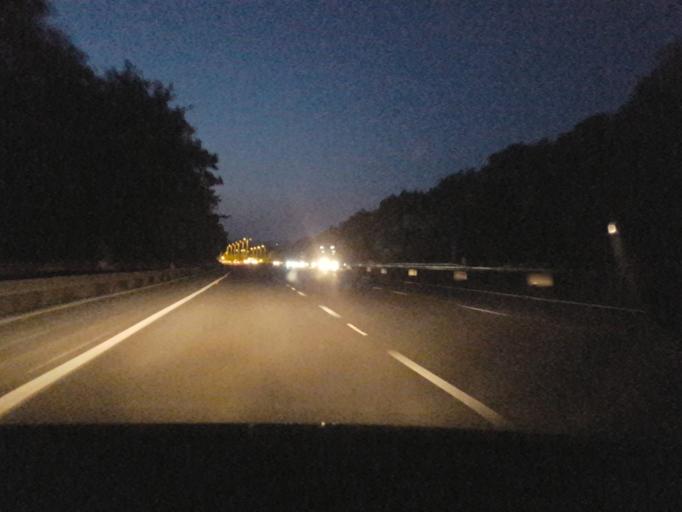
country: GB
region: England
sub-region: Leicestershire
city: Shepshed
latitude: 52.7485
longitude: -1.2759
